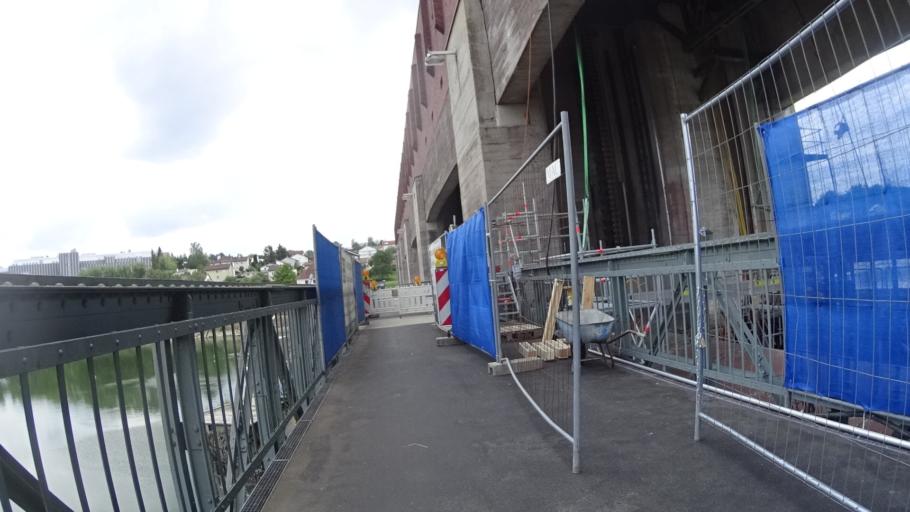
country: DE
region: Bavaria
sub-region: Lower Bavaria
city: Passau
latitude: 48.5786
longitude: 13.4069
